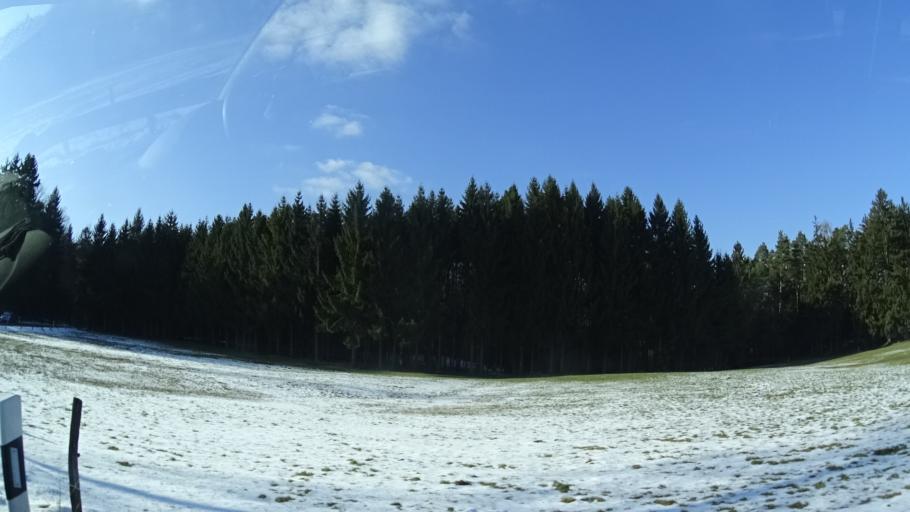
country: DE
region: Hesse
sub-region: Regierungsbezirk Kassel
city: Kalbach
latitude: 50.4127
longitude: 9.7123
